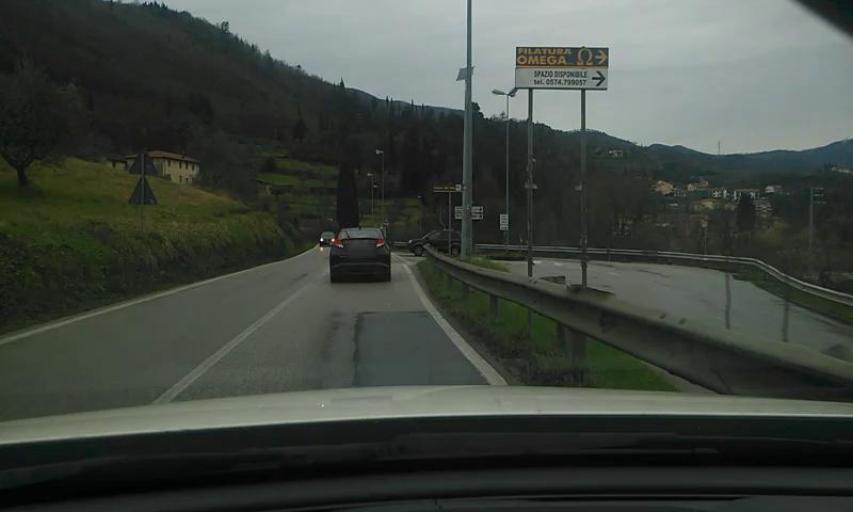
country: IT
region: Tuscany
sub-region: Provincia di Prato
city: Vaiano
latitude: 43.9417
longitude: 11.1266
